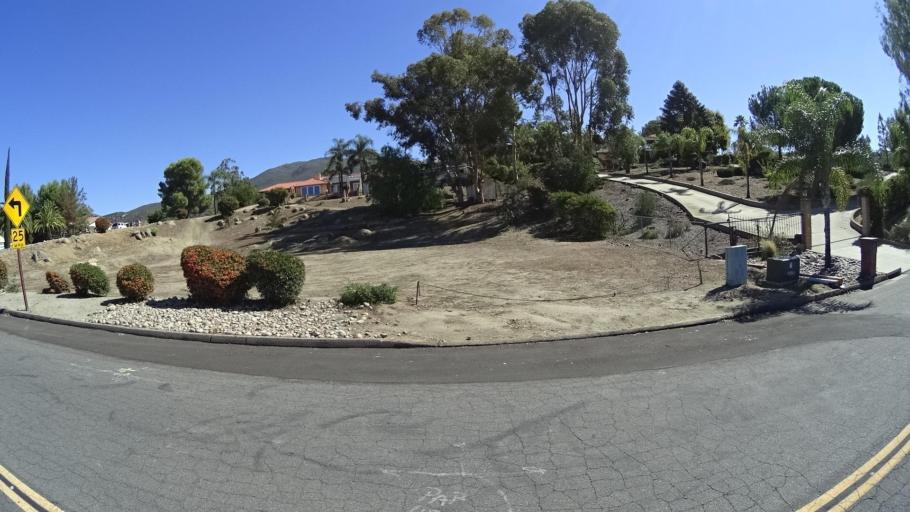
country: US
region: California
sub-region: San Diego County
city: Alpine
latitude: 32.8528
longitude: -116.7634
